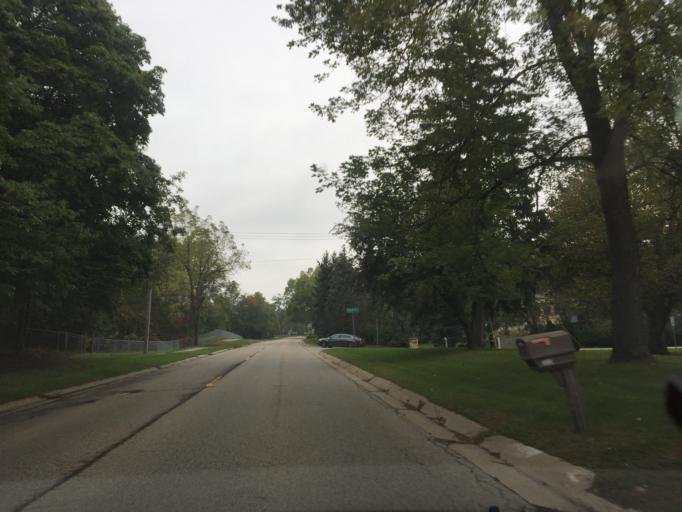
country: US
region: Michigan
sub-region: Oakland County
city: Orchard Lake
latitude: 42.5703
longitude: -83.3348
